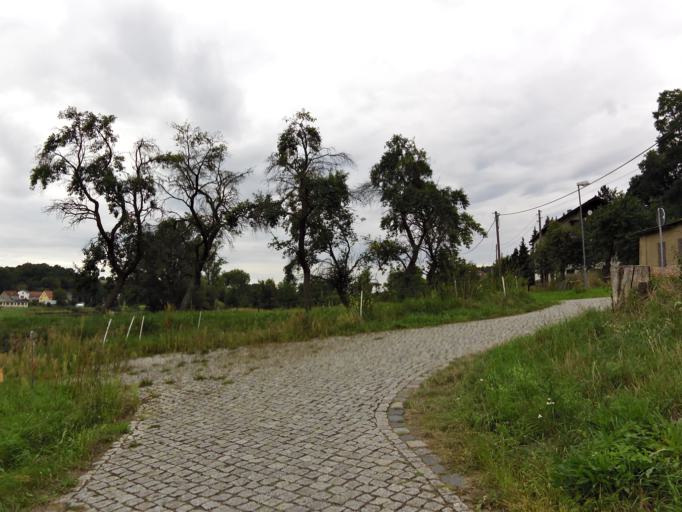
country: DE
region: Saxony
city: Meissen
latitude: 51.2045
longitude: 13.4094
